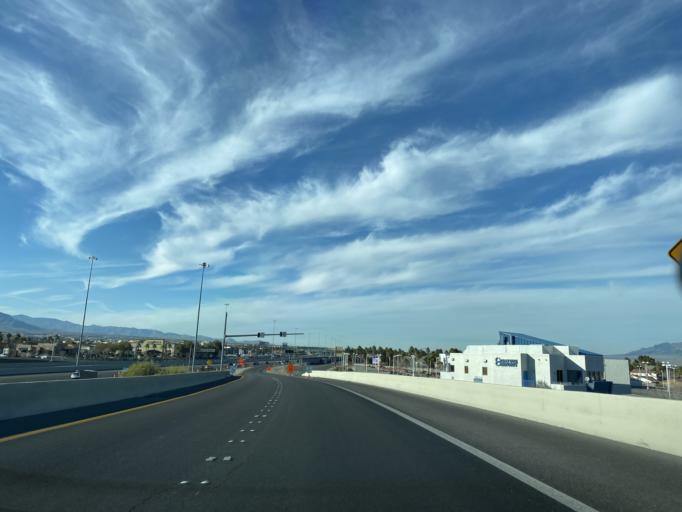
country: US
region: Nevada
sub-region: Clark County
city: Las Vegas
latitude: 36.2638
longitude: -115.2531
